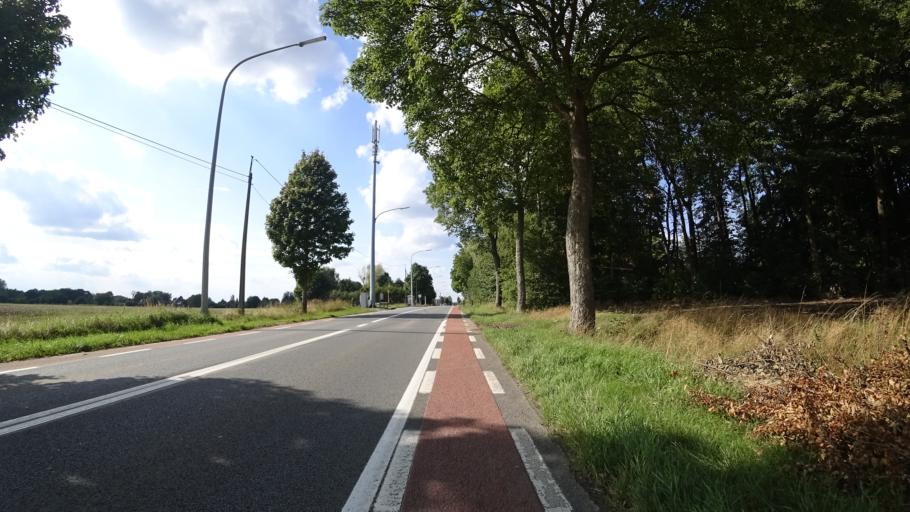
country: BE
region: Wallonia
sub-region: Province de Namur
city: Floreffe
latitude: 50.4795
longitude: 4.7722
